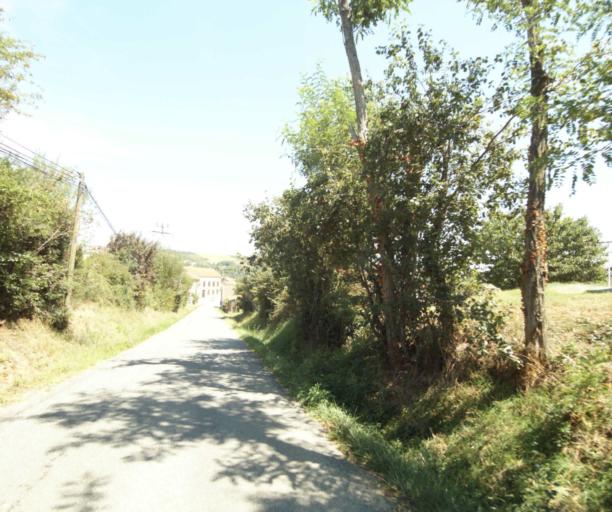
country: FR
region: Midi-Pyrenees
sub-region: Departement de l'Ariege
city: Lezat-sur-Leze
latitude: 43.2767
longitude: 1.3436
